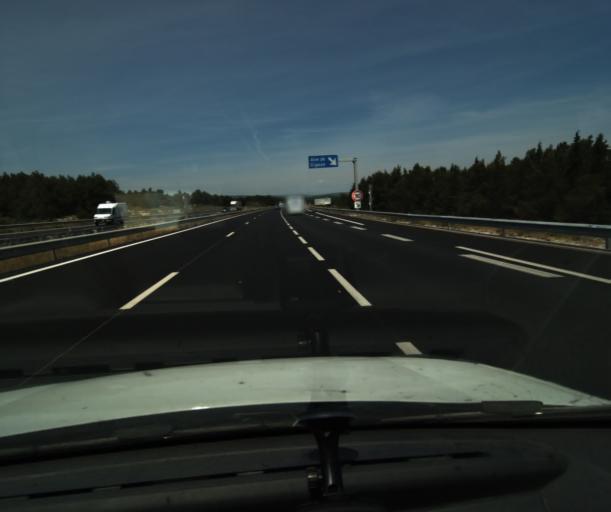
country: FR
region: Languedoc-Roussillon
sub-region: Departement de l'Aude
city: Sigean
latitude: 43.0158
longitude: 2.9521
